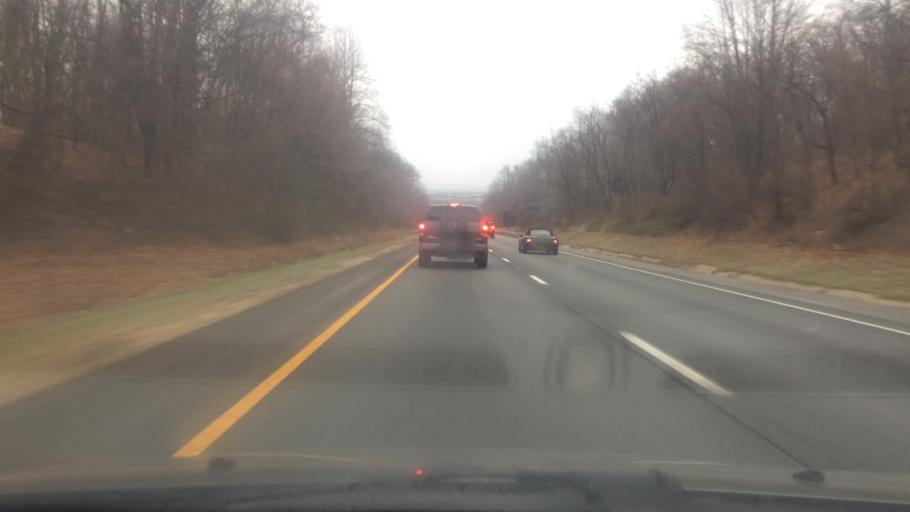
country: US
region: Maryland
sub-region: Washington County
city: Boonsboro
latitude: 39.5595
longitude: -77.6132
